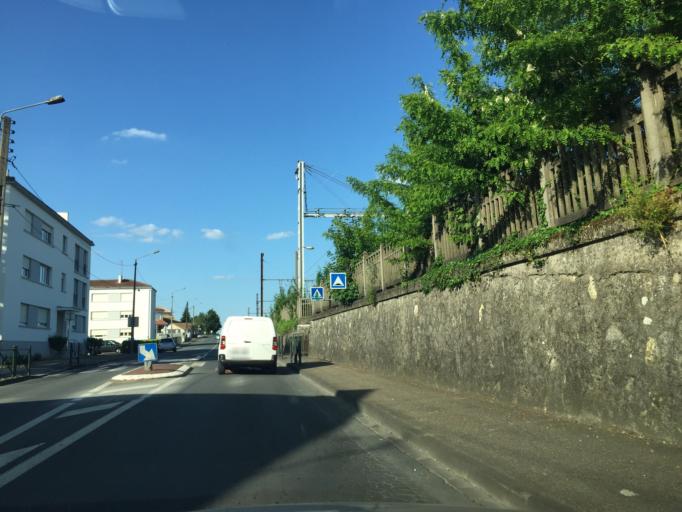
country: FR
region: Aquitaine
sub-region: Departement de la Gironde
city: Coutras
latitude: 45.0382
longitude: -0.1296
